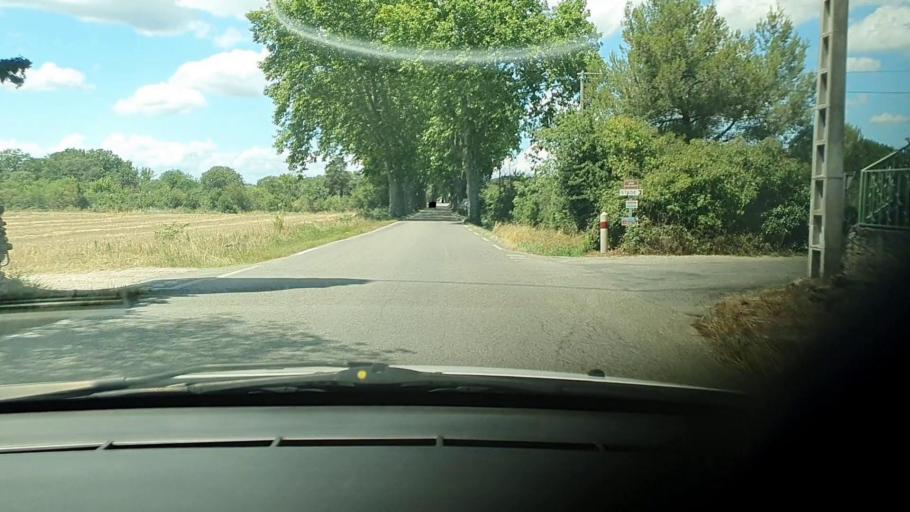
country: FR
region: Languedoc-Roussillon
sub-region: Departement du Gard
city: Montaren-et-Saint-Mediers
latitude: 44.0218
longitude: 4.3962
